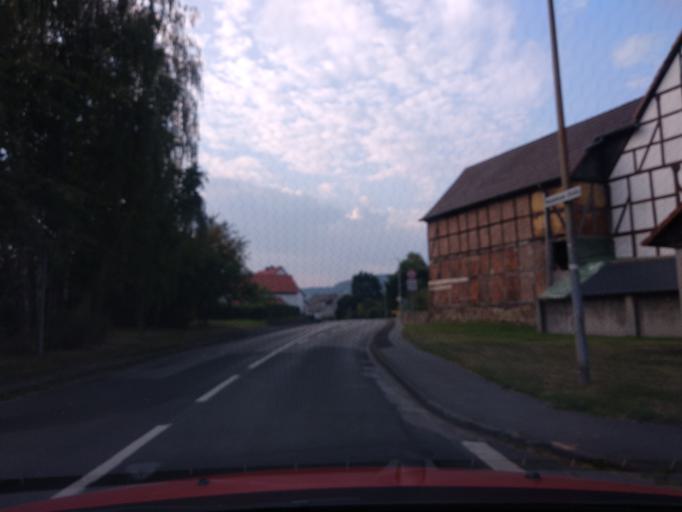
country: DE
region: Hesse
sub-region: Regierungsbezirk Kassel
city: Calden
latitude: 51.3952
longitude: 9.3500
